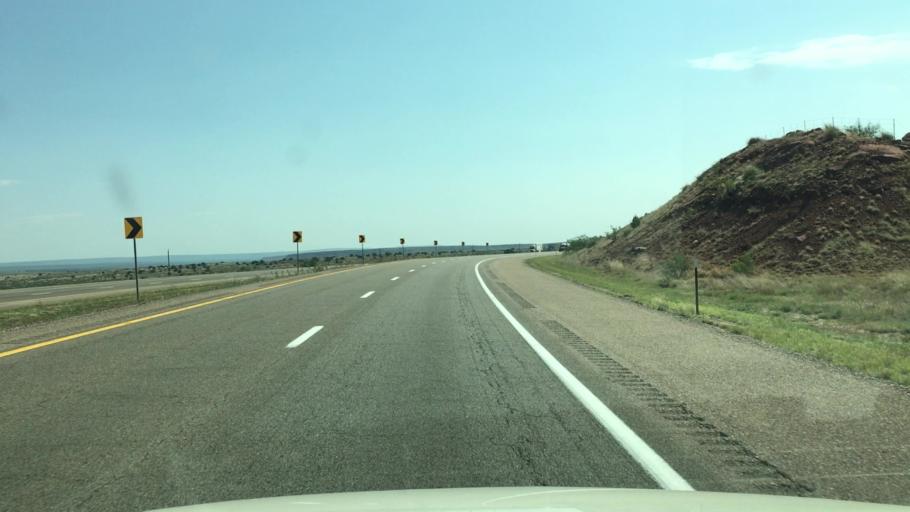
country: US
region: New Mexico
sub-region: Guadalupe County
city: Santa Rosa
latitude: 35.0469
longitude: -104.3768
